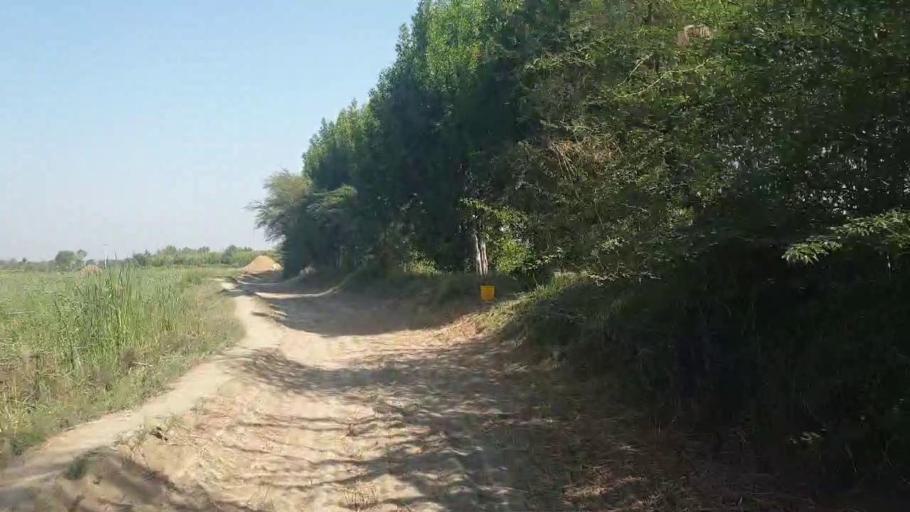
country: PK
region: Sindh
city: Badin
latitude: 24.6813
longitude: 68.8721
